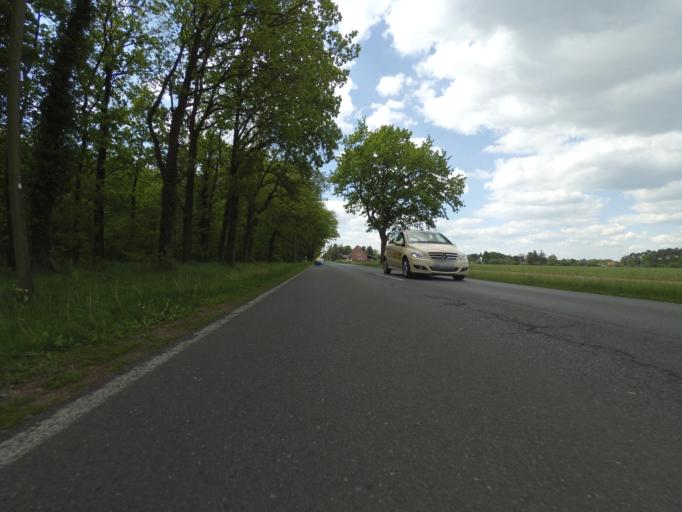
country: DE
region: Lower Saxony
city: Wienhausen
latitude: 52.5948
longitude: 10.2125
